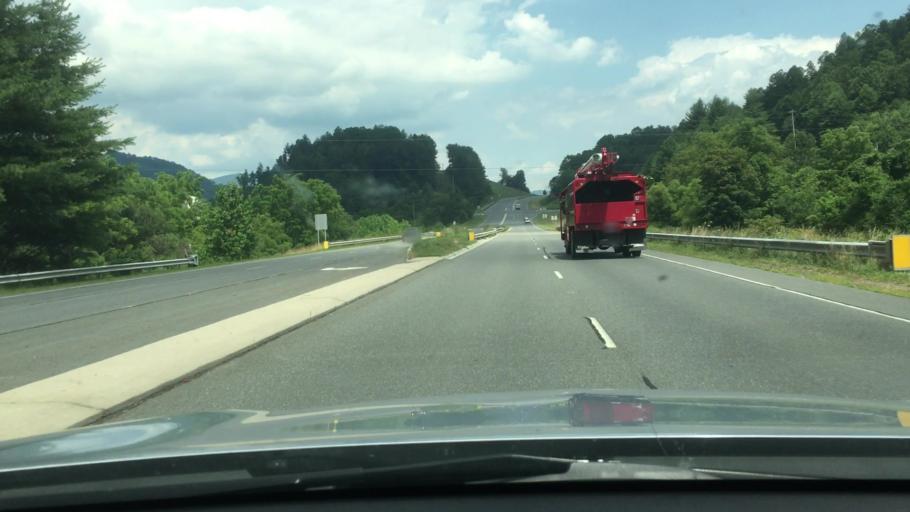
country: US
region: North Carolina
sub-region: Yancey County
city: Burnsville
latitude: 35.9134
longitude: -82.4027
